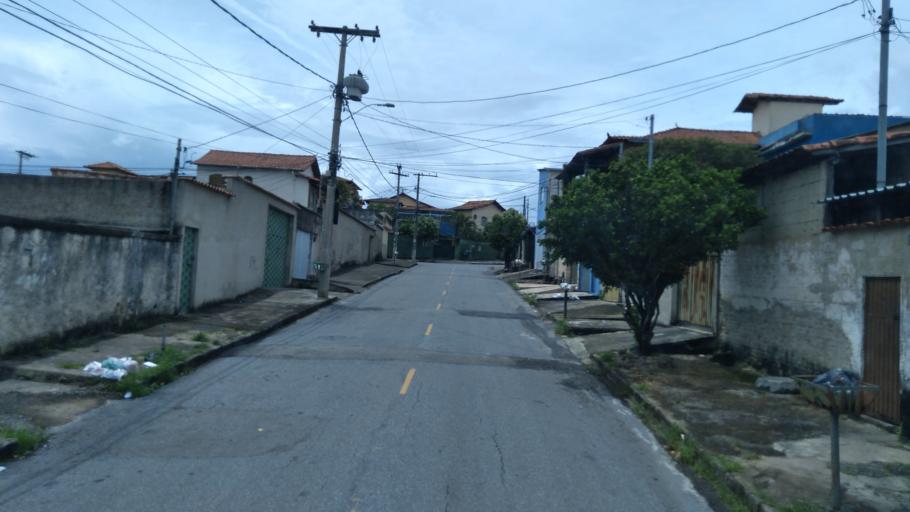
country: BR
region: Minas Gerais
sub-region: Belo Horizonte
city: Belo Horizonte
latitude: -19.8539
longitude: -43.9164
